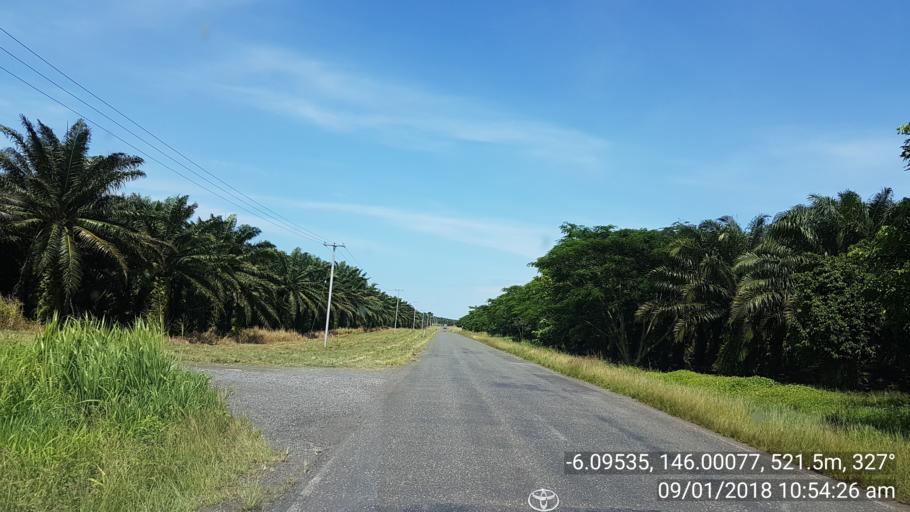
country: PG
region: Eastern Highlands
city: Kainantu
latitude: -6.0956
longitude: 146.0009
